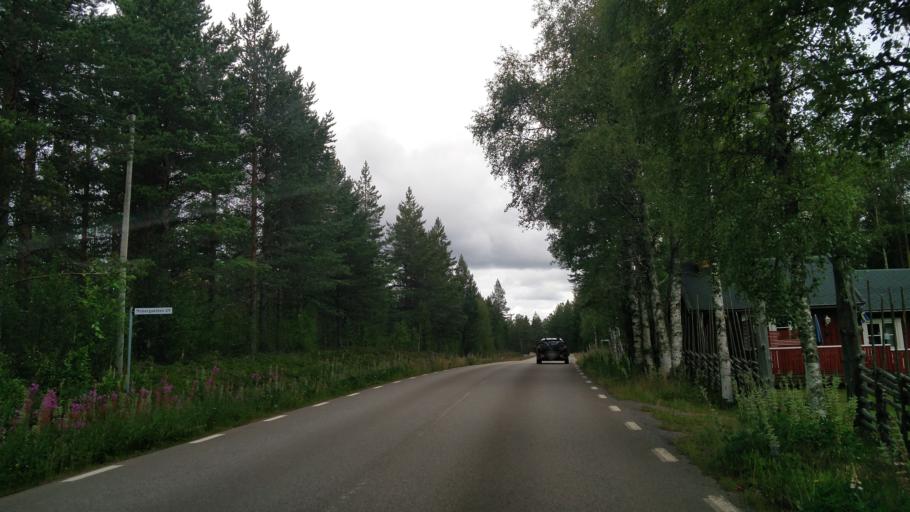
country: NO
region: Hedmark
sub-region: Trysil
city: Innbygda
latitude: 61.1688
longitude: 12.8390
